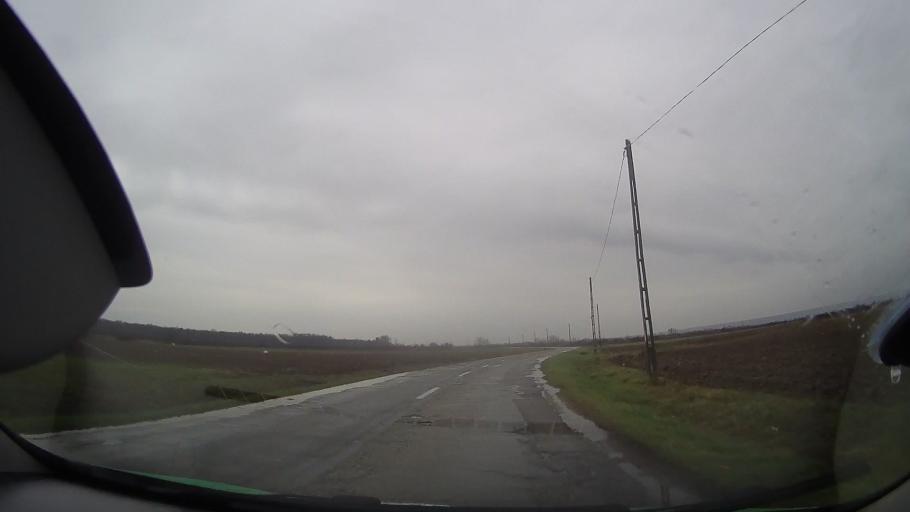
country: RO
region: Bihor
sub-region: Comuna Cociuba Mare
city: Cociuba Mare
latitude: 46.7406
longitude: 21.9830
